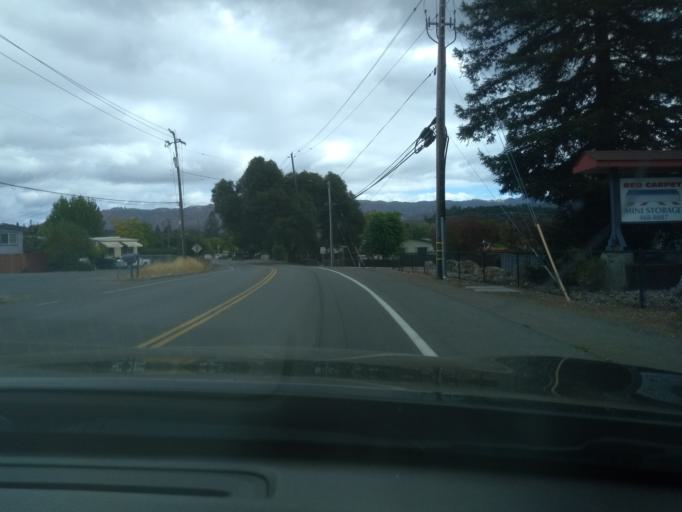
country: US
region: California
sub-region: Mendocino County
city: Ukiah
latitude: 39.1928
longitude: -123.2061
